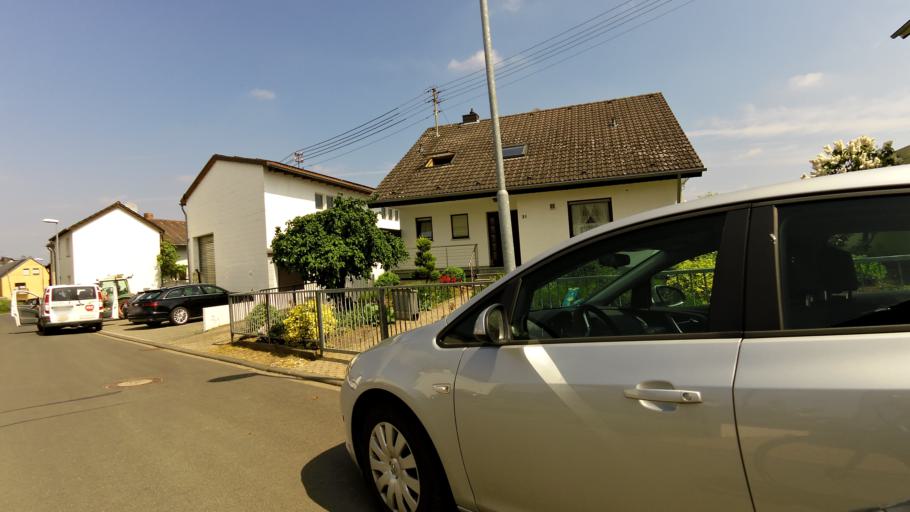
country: DE
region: North Rhine-Westphalia
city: Meckenheim
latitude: 50.6060
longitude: 6.9923
